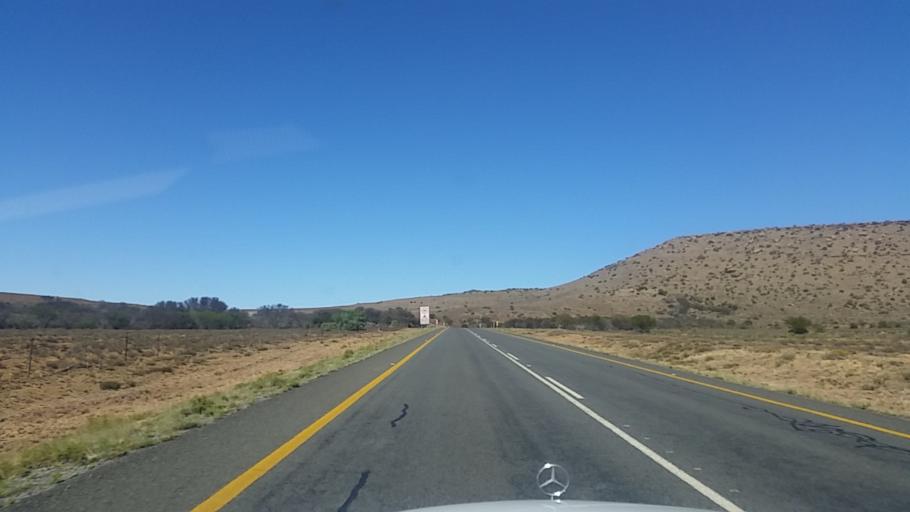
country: ZA
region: Eastern Cape
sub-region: Cacadu District Municipality
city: Graaff-Reinet
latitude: -31.9432
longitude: 24.7299
